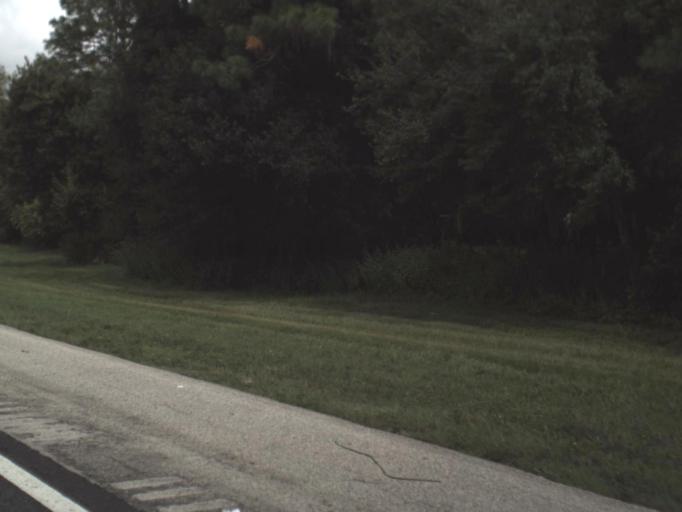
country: US
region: Florida
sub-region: Manatee County
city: Ellenton
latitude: 27.4828
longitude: -82.4679
